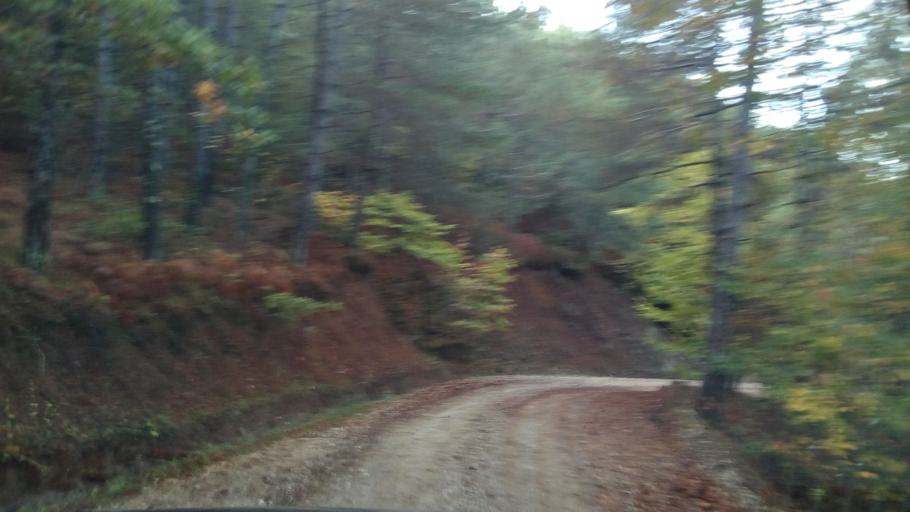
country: GR
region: West Greece
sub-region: Nomos Achaias
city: Kamarai
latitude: 38.4797
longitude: 22.0238
